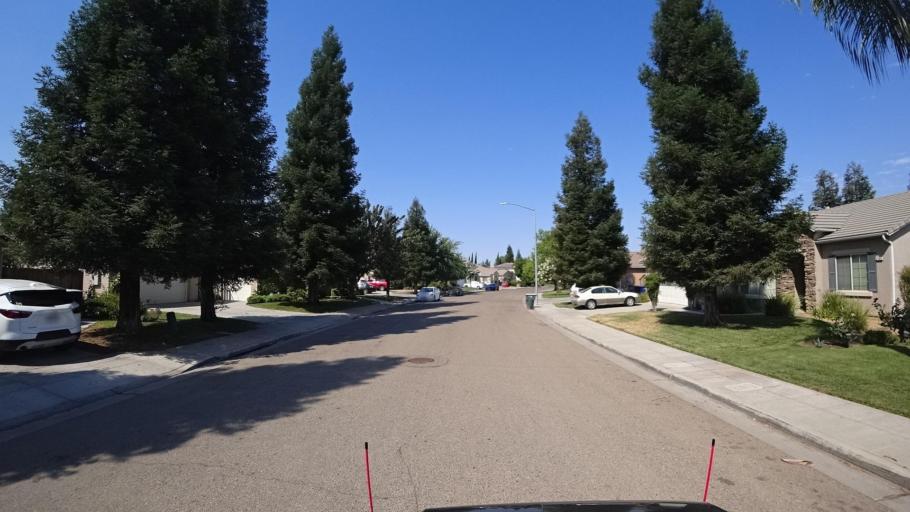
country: US
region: California
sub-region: Fresno County
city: Sunnyside
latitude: 36.7209
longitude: -119.6917
